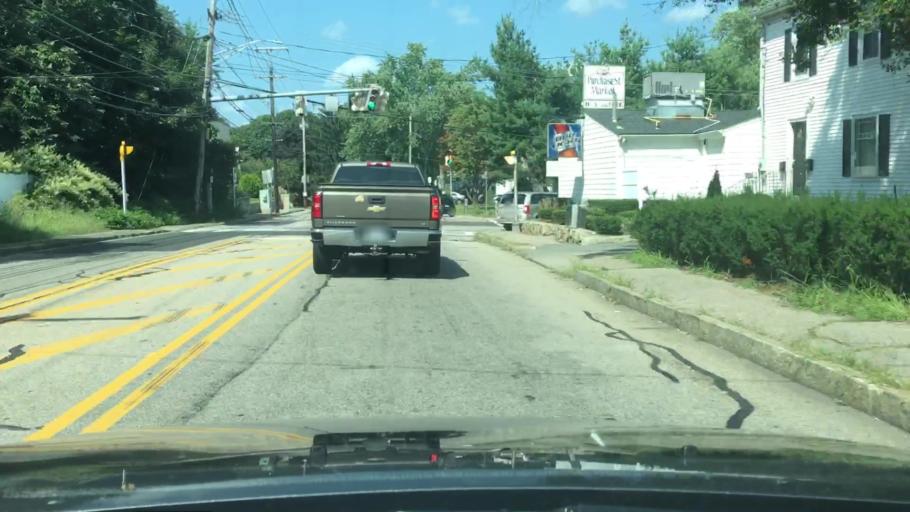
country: US
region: Massachusetts
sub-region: Worcester County
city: Milford
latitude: 42.1547
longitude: -71.5231
